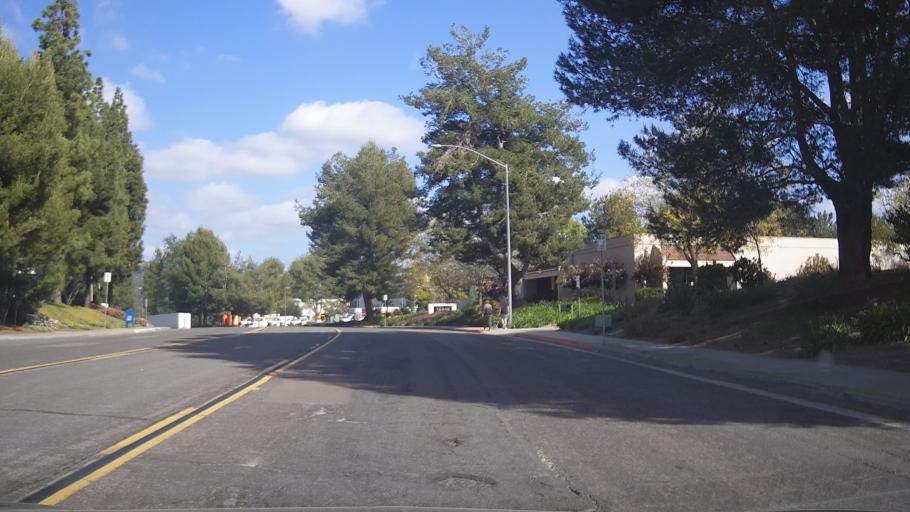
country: US
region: California
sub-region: San Diego County
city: Poway
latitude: 32.9872
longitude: -117.0700
